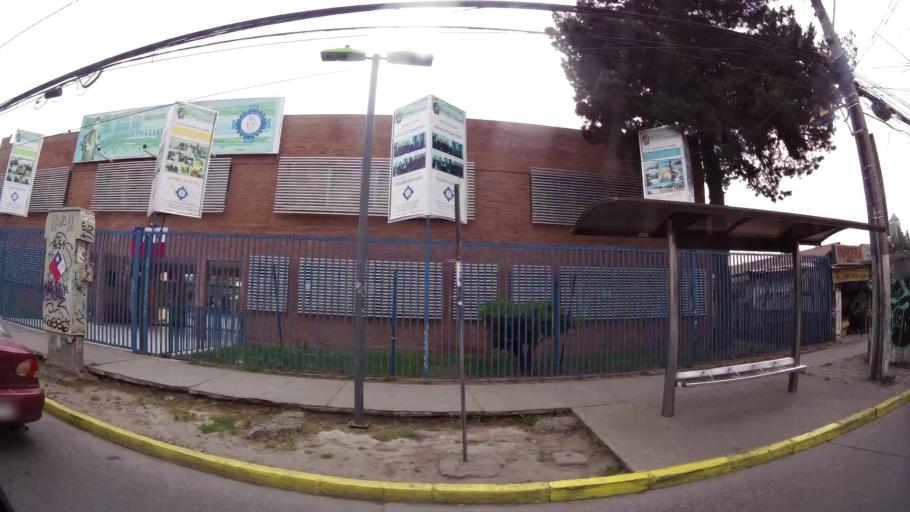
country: CL
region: Santiago Metropolitan
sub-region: Provincia de Santiago
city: Lo Prado
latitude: -33.5150
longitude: -70.7635
